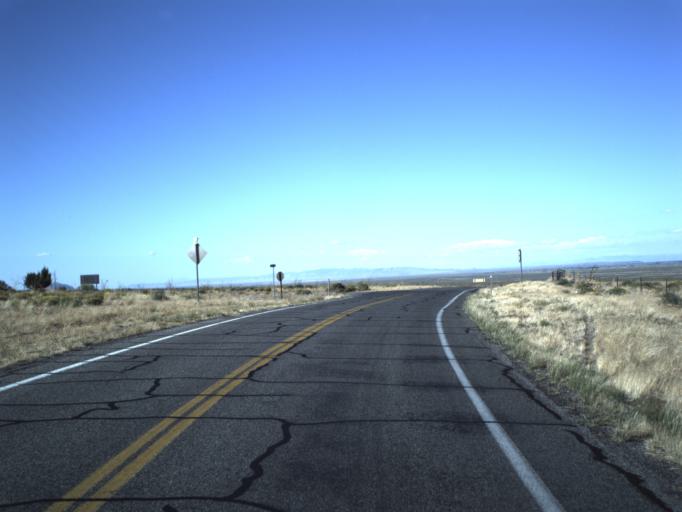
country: US
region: Utah
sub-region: Millard County
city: Delta
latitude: 39.3559
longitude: -112.3620
